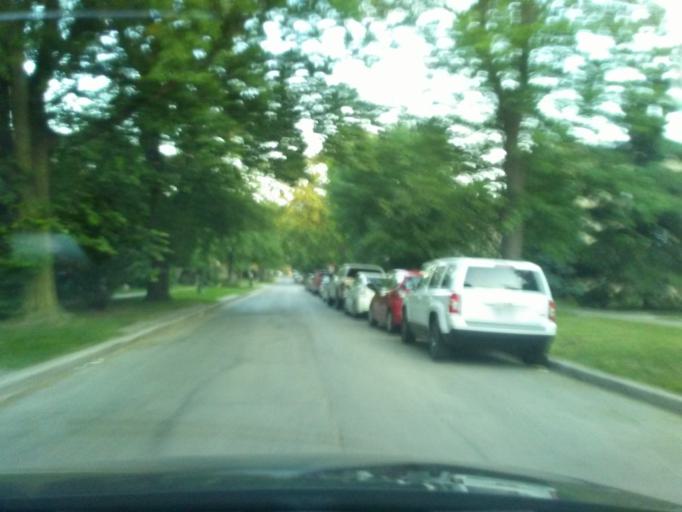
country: US
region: Illinois
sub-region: Cook County
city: Evanston
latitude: 42.0230
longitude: -87.6818
